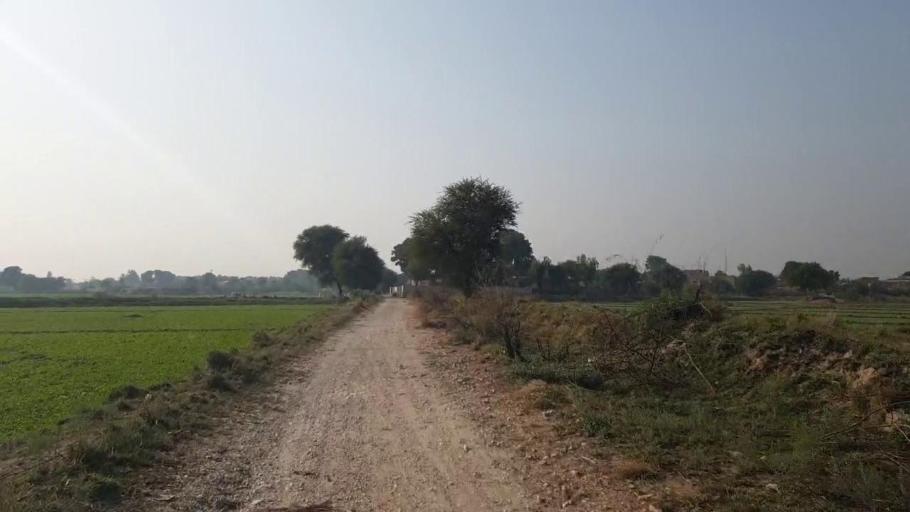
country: PK
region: Sindh
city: Kotri
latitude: 25.3389
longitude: 68.3212
